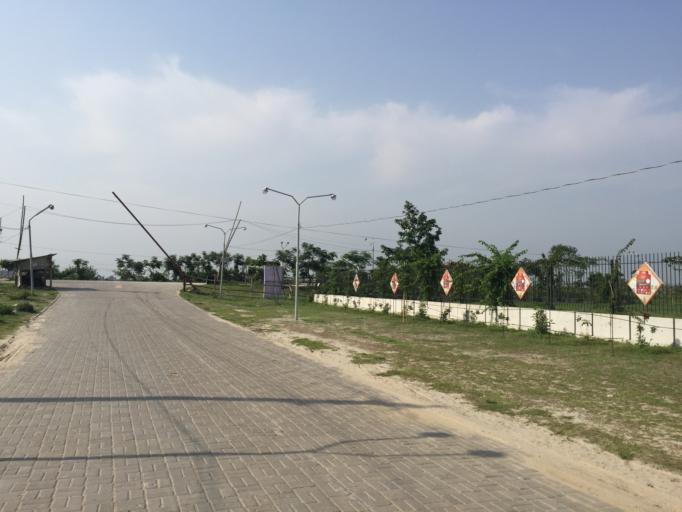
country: BD
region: Dhaka
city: Paltan
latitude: 23.7998
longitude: 90.4488
